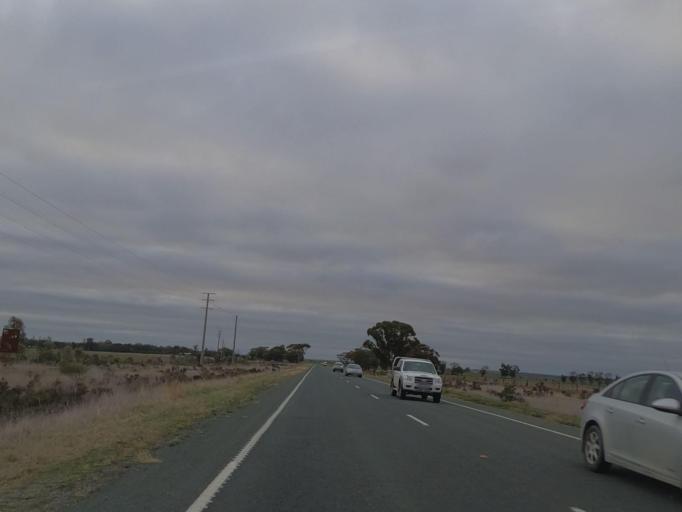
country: AU
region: Victoria
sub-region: Swan Hill
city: Swan Hill
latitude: -35.5669
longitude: 143.7844
